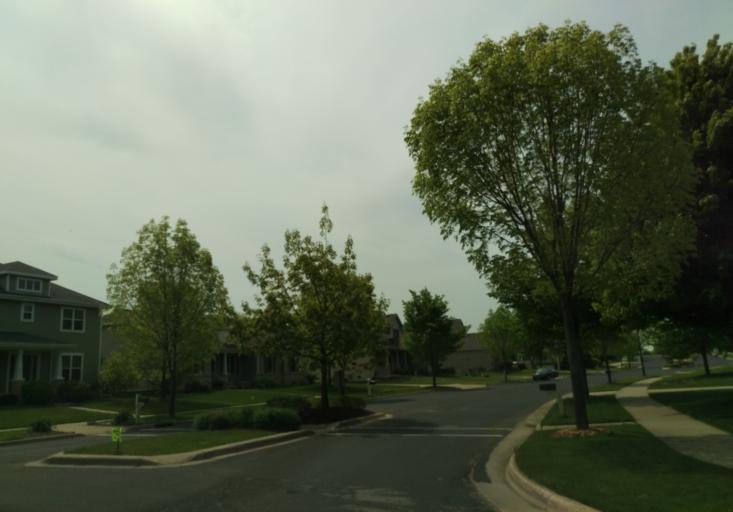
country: US
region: Wisconsin
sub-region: Dane County
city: Monona
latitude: 43.0869
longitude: -89.2737
